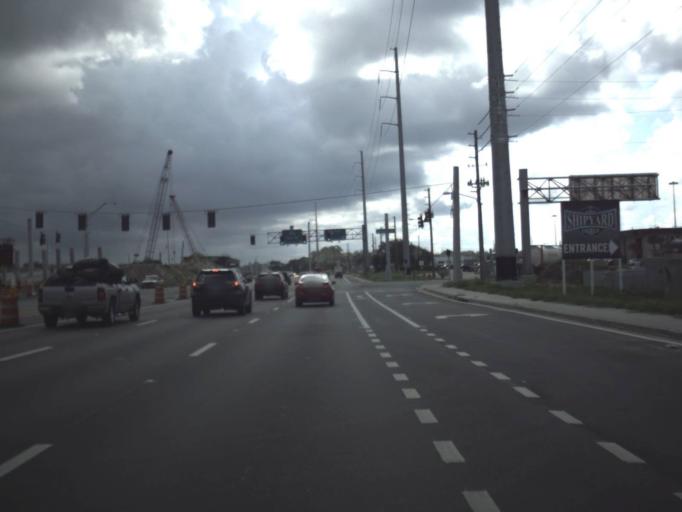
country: US
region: Florida
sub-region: Bay County
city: Upper Grand Lagoon
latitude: 30.1851
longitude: -85.7321
